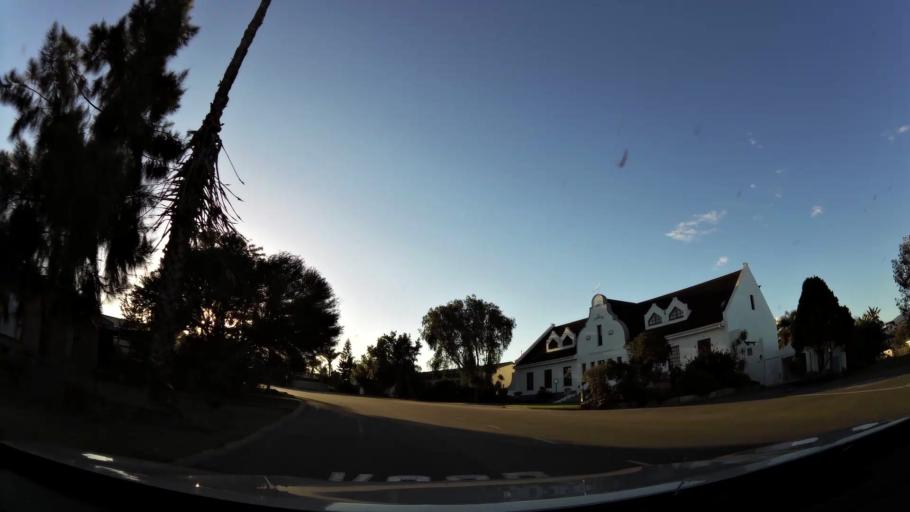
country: ZA
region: Western Cape
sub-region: Eden District Municipality
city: Riversdale
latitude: -34.0857
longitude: 21.2476
